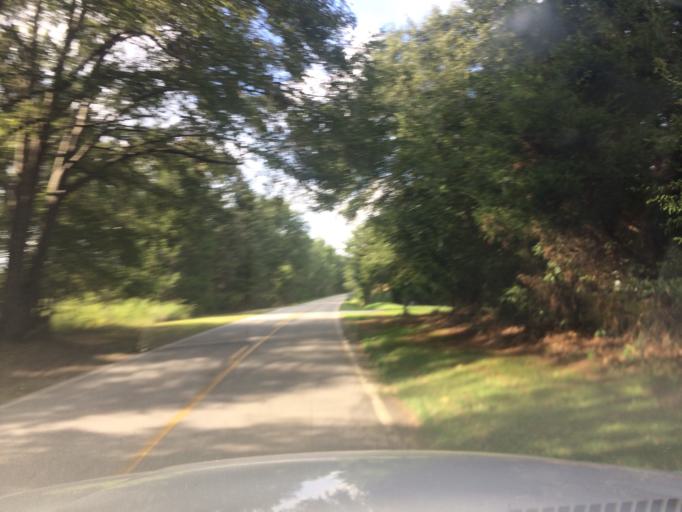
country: US
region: South Carolina
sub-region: Spartanburg County
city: Woodruff
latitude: 34.7790
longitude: -82.1126
